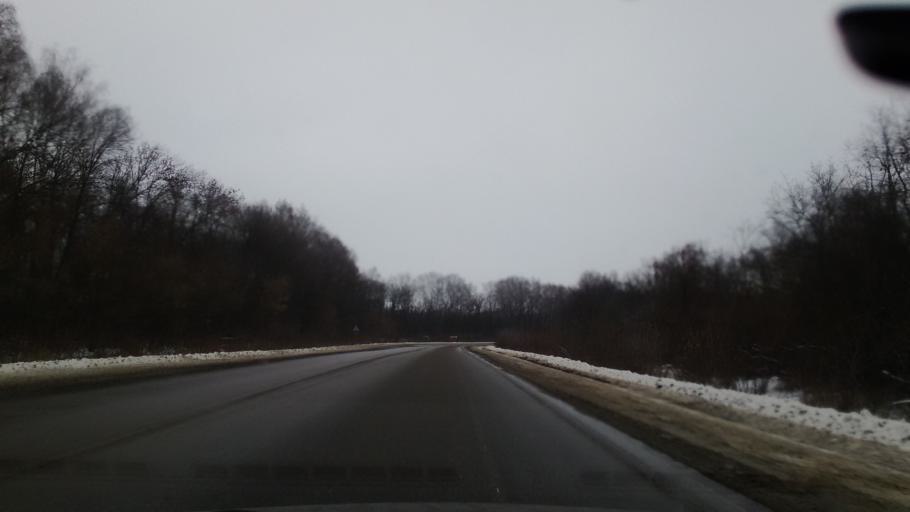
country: RU
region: Tula
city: Bolokhovo
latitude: 54.0486
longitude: 37.8444
